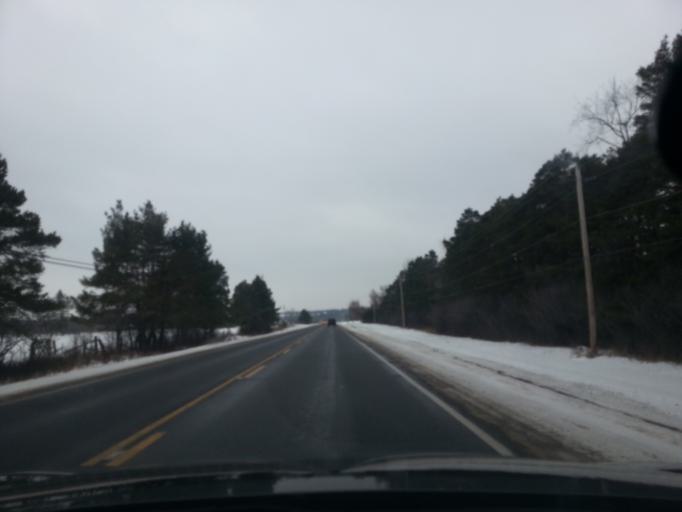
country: CA
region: Ontario
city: Carleton Place
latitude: 45.2748
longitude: -76.1176
